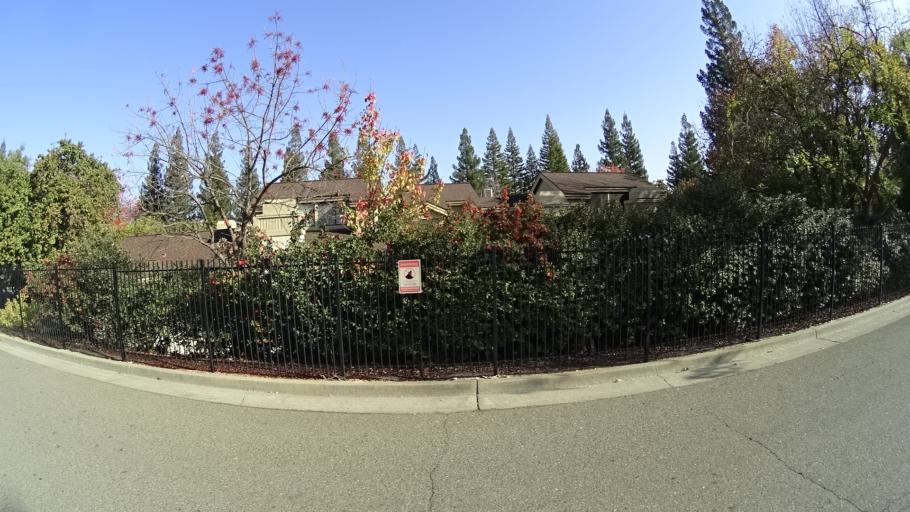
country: US
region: California
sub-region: Sacramento County
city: Citrus Heights
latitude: 38.7027
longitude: -121.2486
